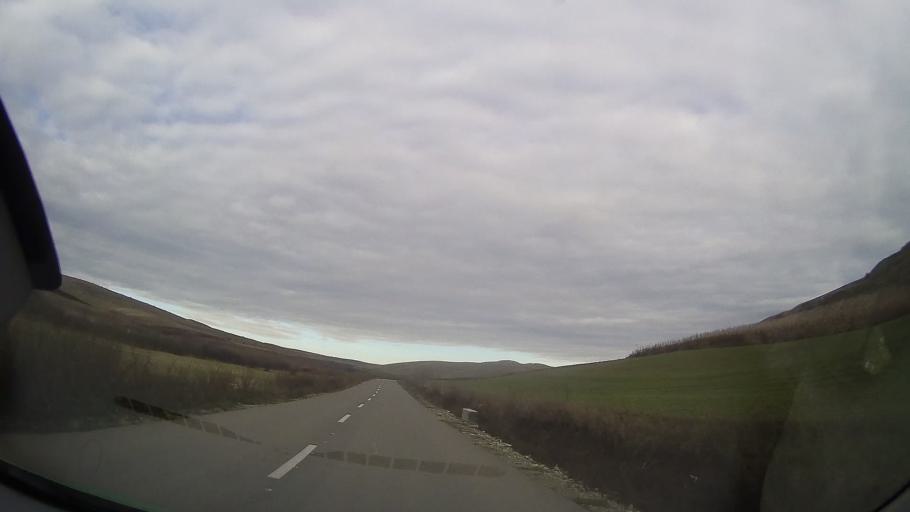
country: RO
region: Bistrita-Nasaud
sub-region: Comuna Silvasu de Campie
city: Silvasu de Campie
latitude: 46.7969
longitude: 24.2959
